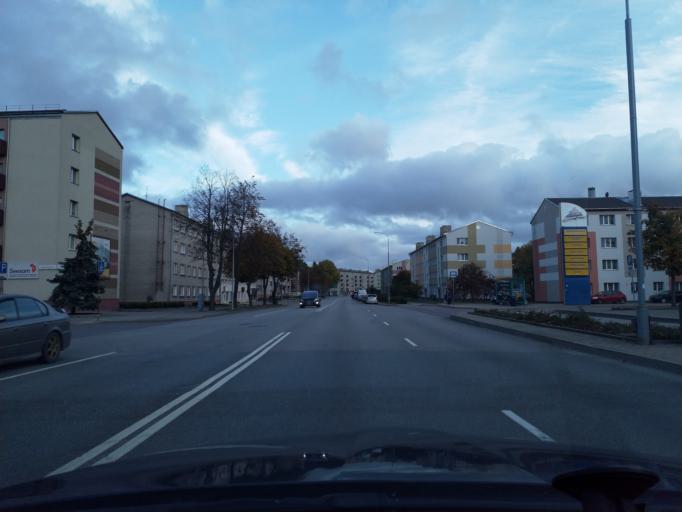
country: LV
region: Ventspils
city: Ventspils
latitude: 57.3897
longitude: 21.5693
